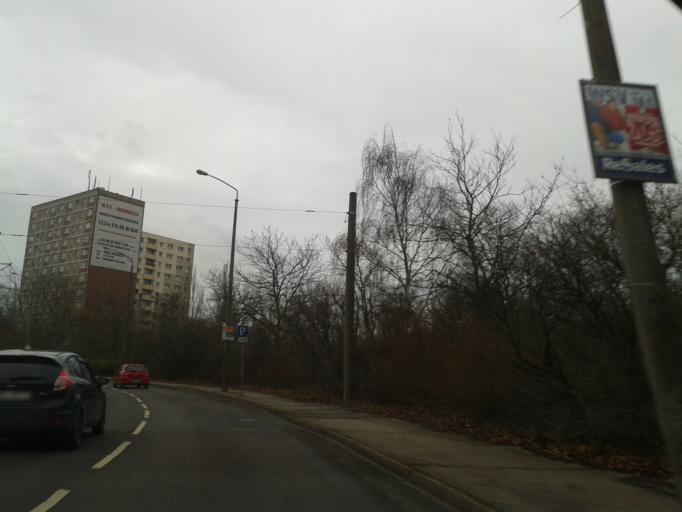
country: DE
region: Saxony-Anhalt
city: Angersdorf
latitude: 51.4517
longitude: 11.9430
